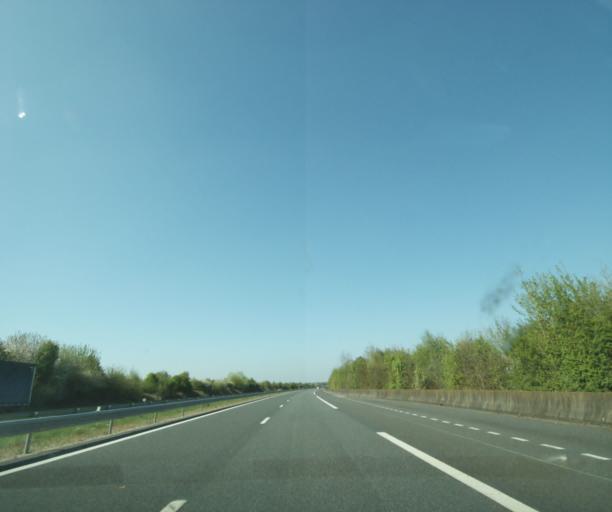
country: FR
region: Centre
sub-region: Departement du Loiret
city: Vimory
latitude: 47.9410
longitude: 2.6749
